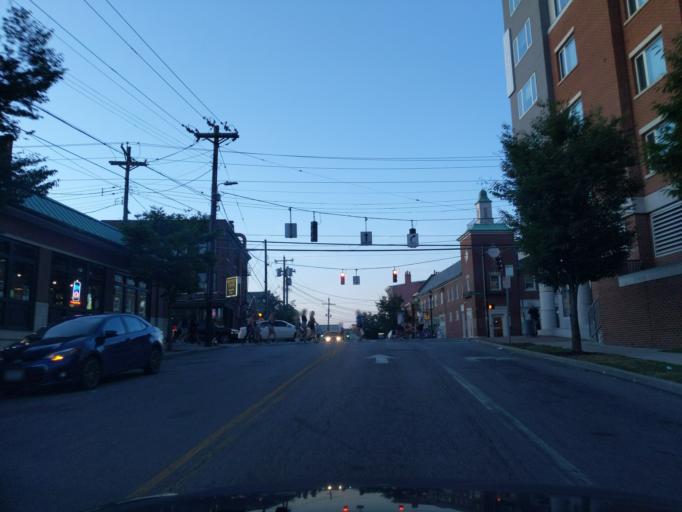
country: US
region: Kentucky
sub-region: Campbell County
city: Newport
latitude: 39.1275
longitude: -84.5193
